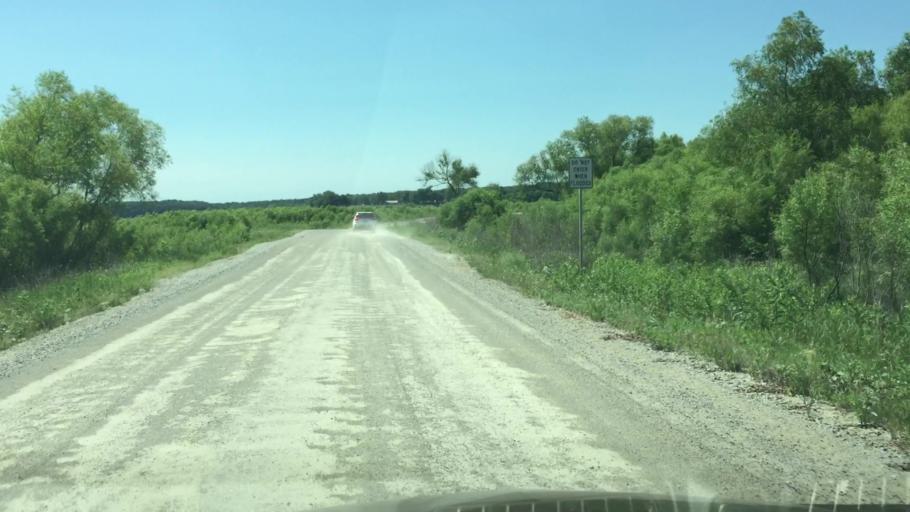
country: US
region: Iowa
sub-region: Linn County
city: Ely
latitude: 41.8170
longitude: -91.5889
